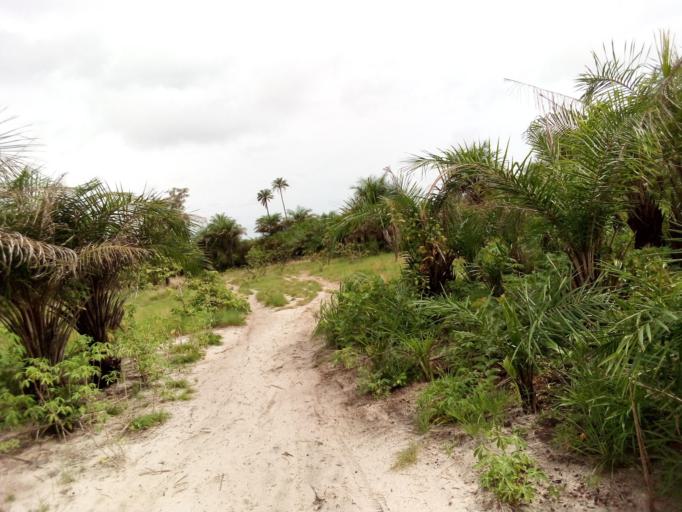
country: SL
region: Southern Province
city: Bonthe
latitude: 7.5196
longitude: -12.5717
